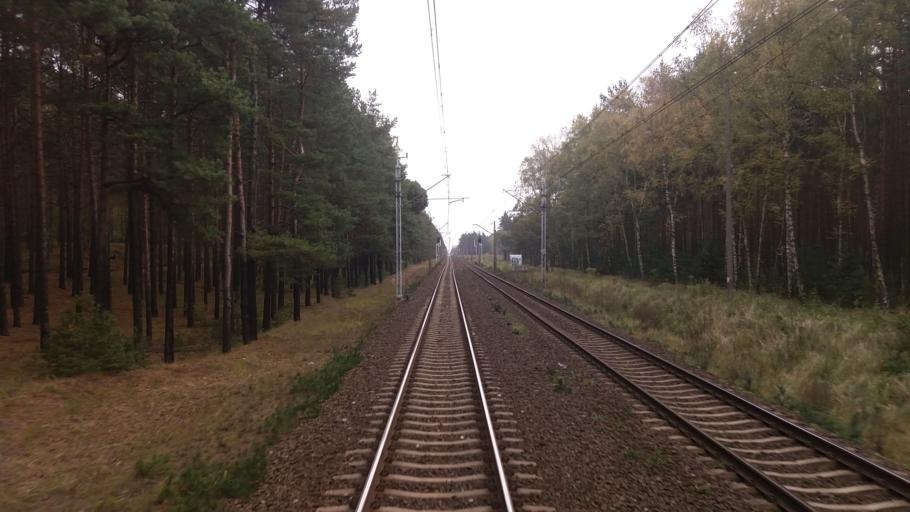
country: PL
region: West Pomeranian Voivodeship
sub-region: Powiat stargardzki
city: Kobylanka
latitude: 53.3812
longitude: 14.7823
